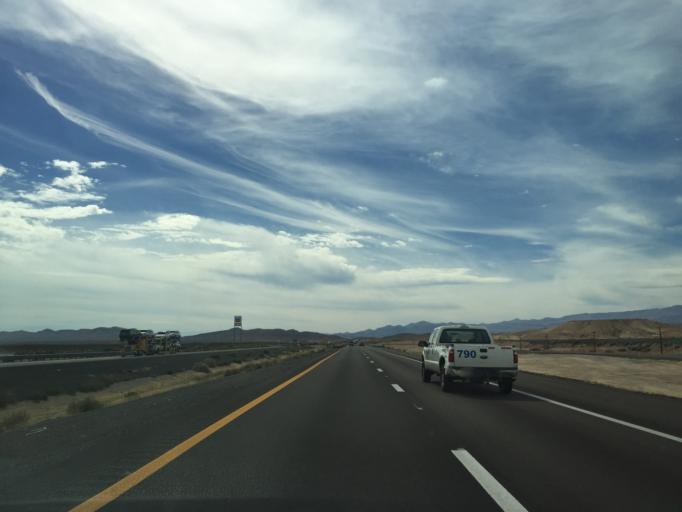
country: US
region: Nevada
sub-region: Clark County
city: Moapa Town
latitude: 36.5038
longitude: -114.7590
